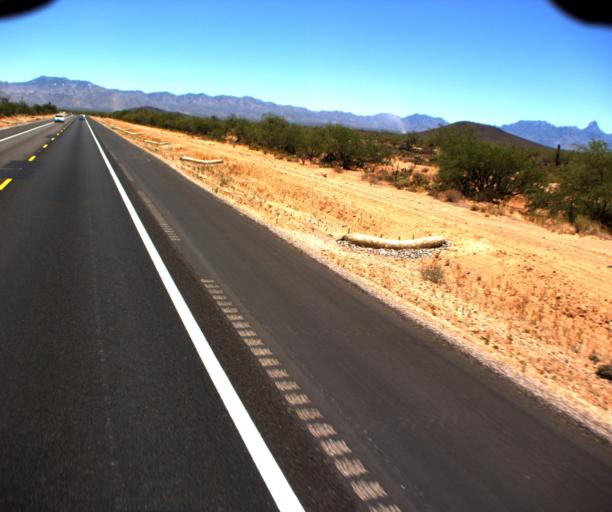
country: US
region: Arizona
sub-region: Pima County
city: Sells
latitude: 31.9189
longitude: -111.8347
